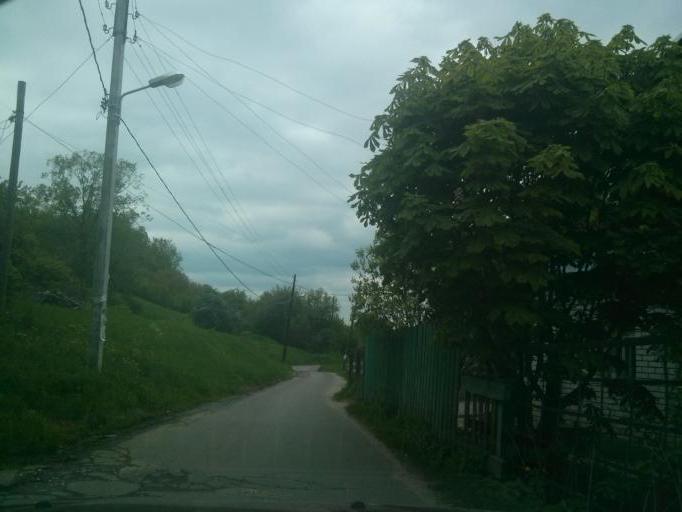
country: RU
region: Nizjnij Novgorod
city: Afonino
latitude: 56.2950
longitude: 44.0978
